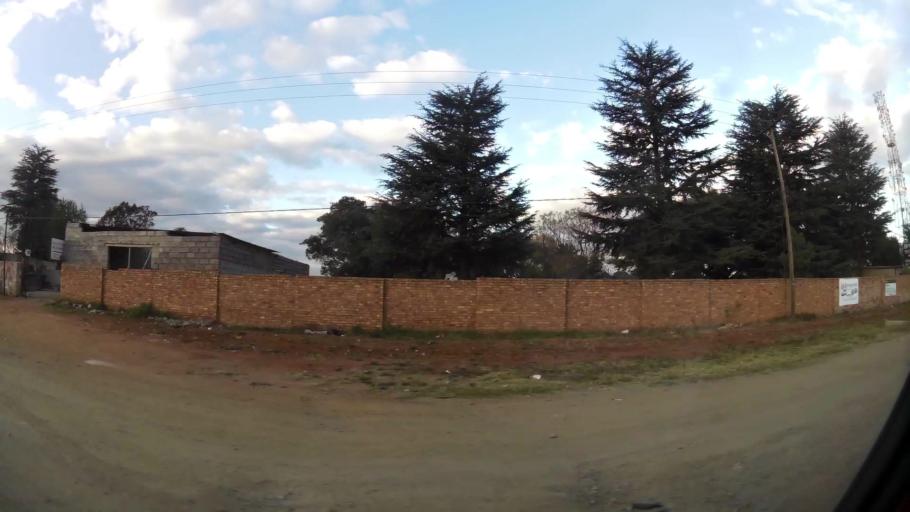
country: ZA
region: Gauteng
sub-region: City of Johannesburg Metropolitan Municipality
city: Midrand
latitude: -26.0054
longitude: 28.1582
